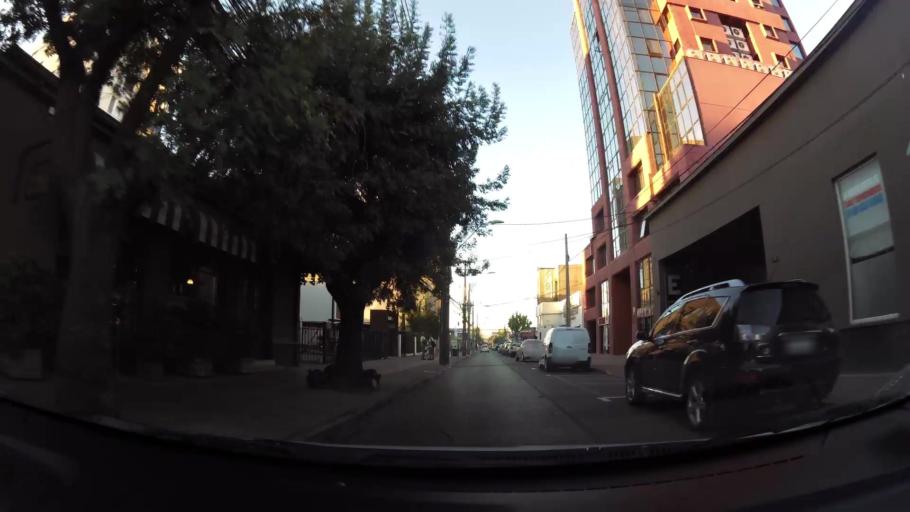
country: CL
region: Maule
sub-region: Provincia de Curico
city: Curico
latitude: -34.9832
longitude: -71.2390
